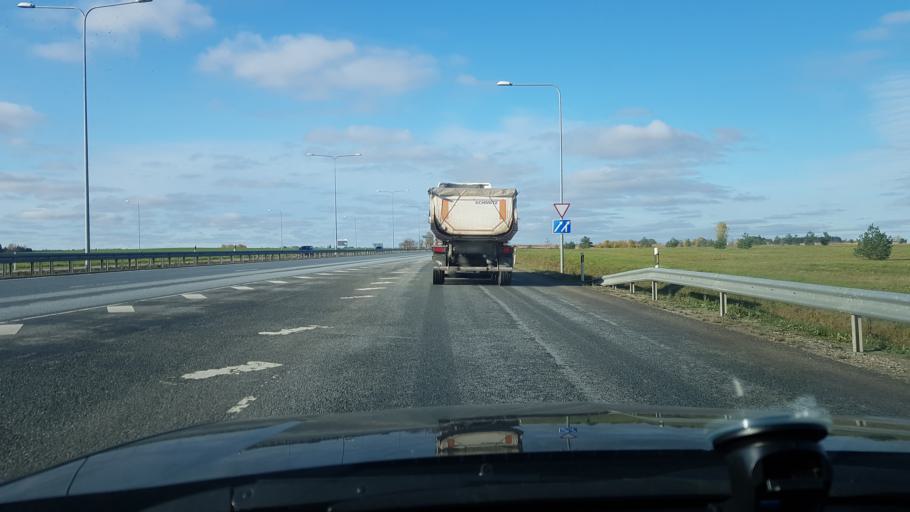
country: EE
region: Laeaene-Virumaa
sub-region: Haljala vald
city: Haljala
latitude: 59.4242
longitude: 26.2686
